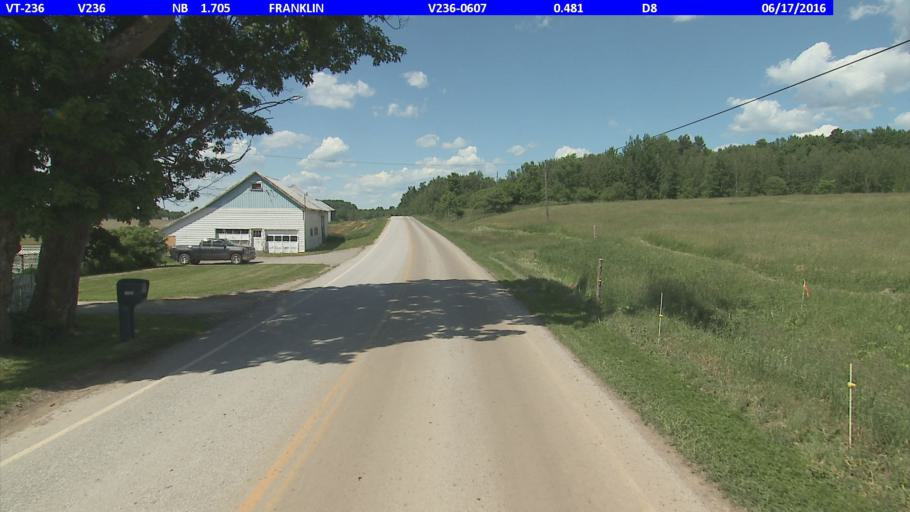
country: US
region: Vermont
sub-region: Franklin County
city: Enosburg Falls
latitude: 44.9352
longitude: -72.8641
